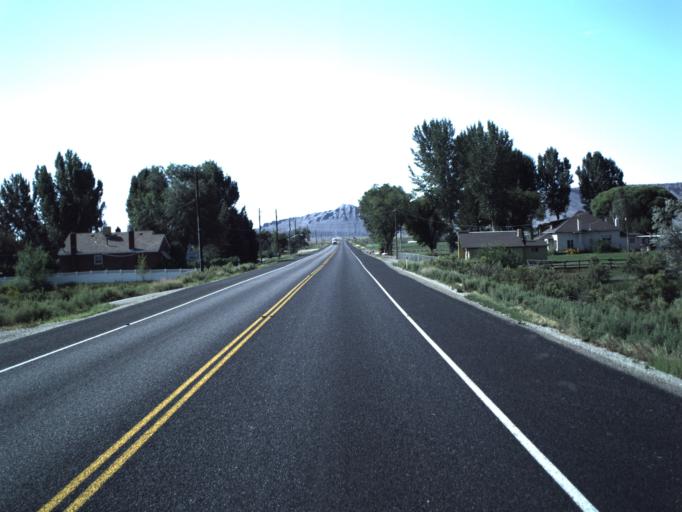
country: US
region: Utah
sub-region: Emery County
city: Ferron
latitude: 39.0717
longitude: -111.1316
